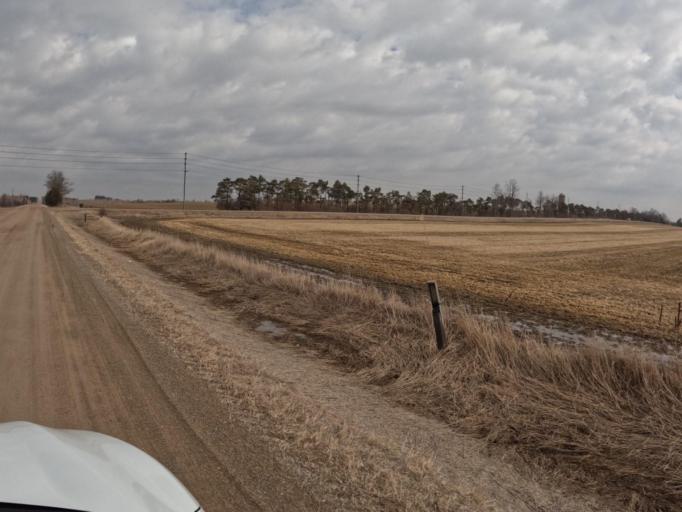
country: CA
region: Ontario
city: Orangeville
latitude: 43.9280
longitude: -80.1873
